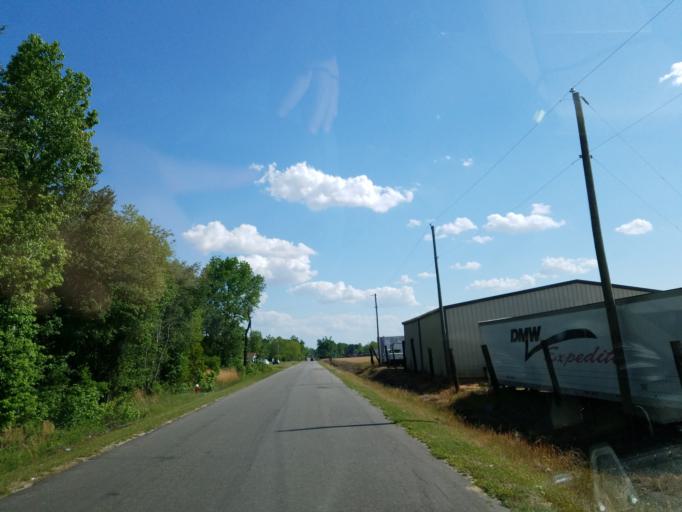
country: US
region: Georgia
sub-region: Dooly County
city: Unadilla
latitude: 32.2041
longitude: -83.7596
